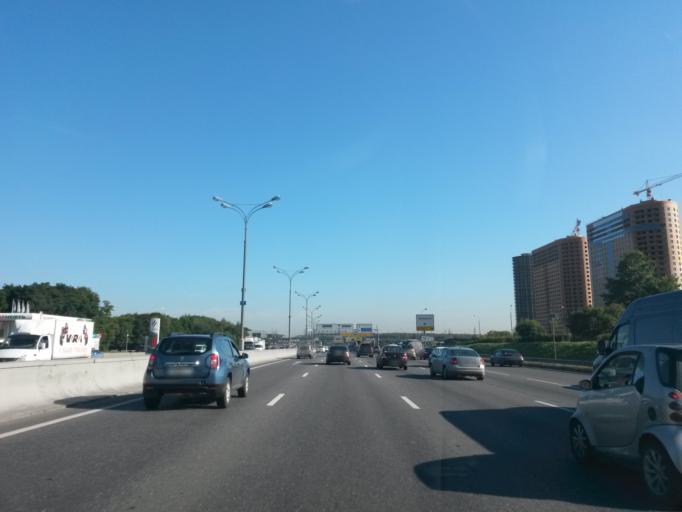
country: RU
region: Moscow
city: Ivanovskoye
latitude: 55.7695
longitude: 37.8433
